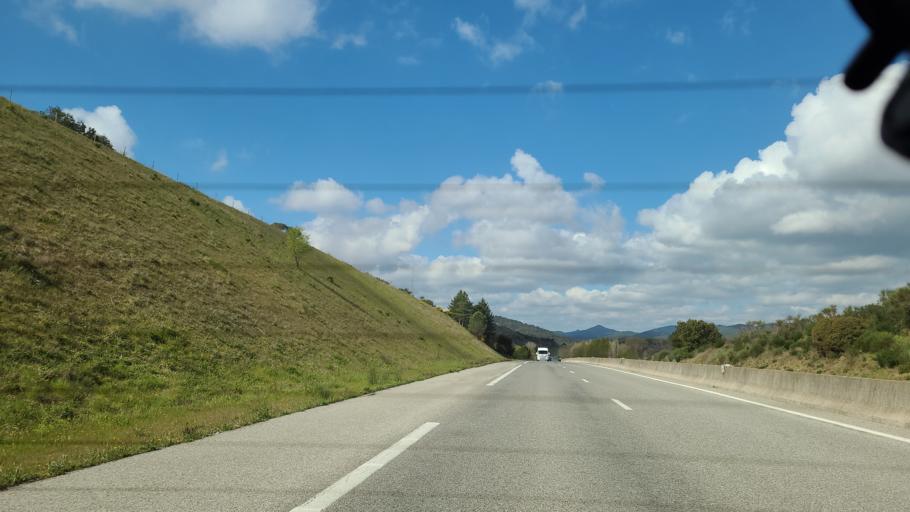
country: FR
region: Provence-Alpes-Cote d'Azur
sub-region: Departement du Var
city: Pignans
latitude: 43.2893
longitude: 6.2229
